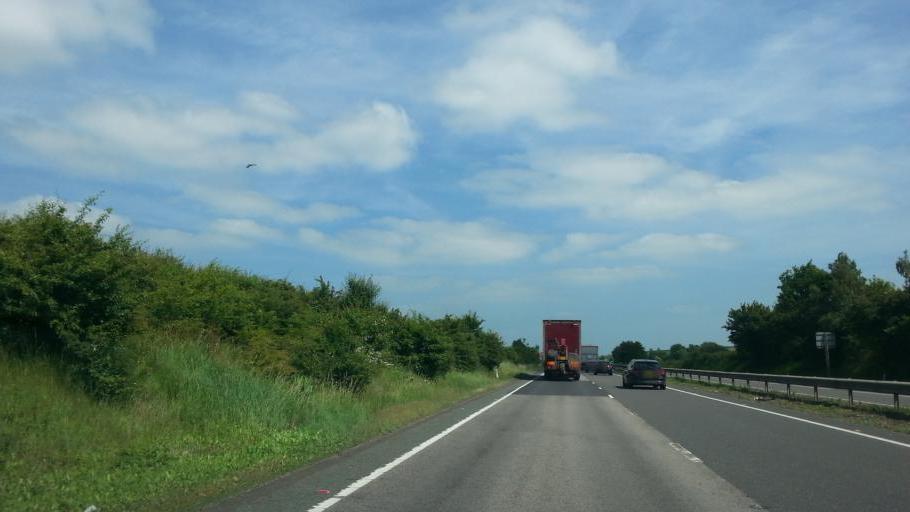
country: GB
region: England
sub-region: Bedford
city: Swineshead
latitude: 52.3647
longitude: -0.4366
